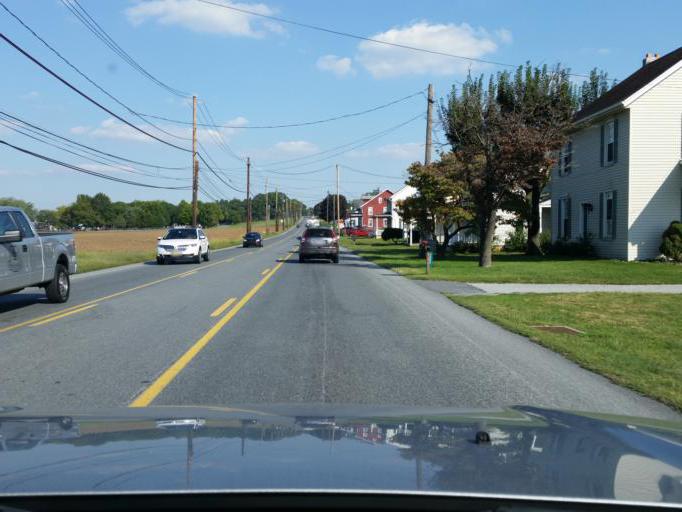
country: US
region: Pennsylvania
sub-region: Lancaster County
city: Gap
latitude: 39.9983
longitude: -76.0602
